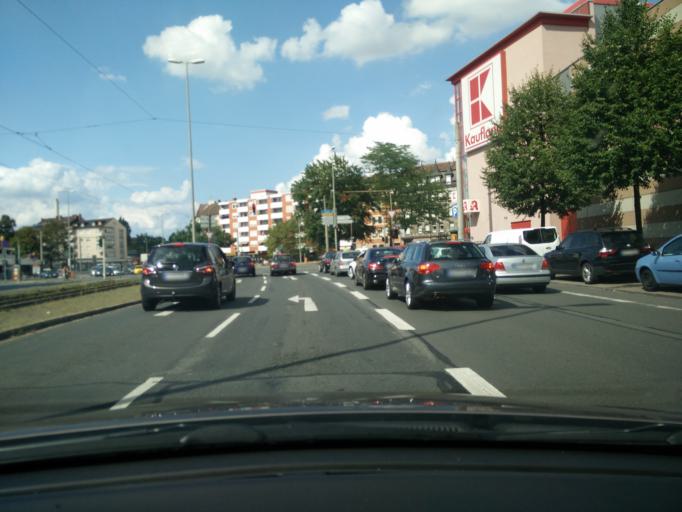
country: DE
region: Bavaria
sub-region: Regierungsbezirk Mittelfranken
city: Nuernberg
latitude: 49.4273
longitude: 11.0656
